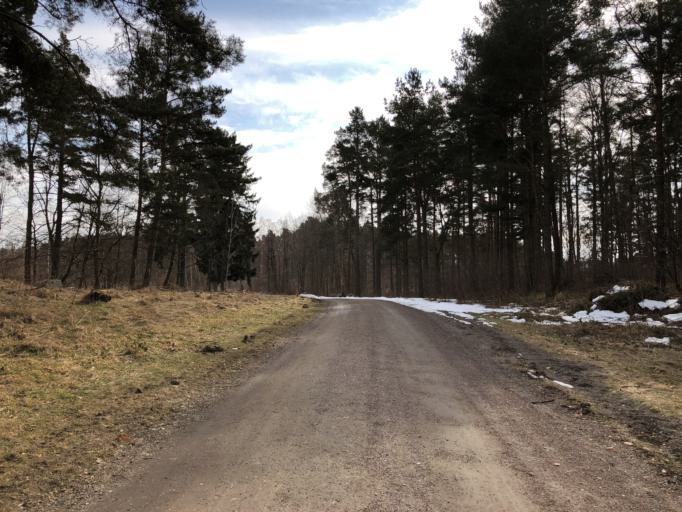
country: SE
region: Kalmar
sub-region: Kalmar Kommun
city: Kalmar
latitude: 56.6578
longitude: 16.3202
